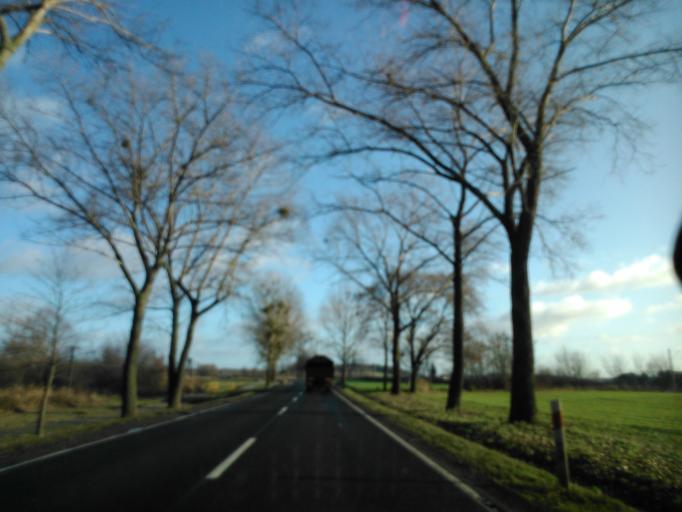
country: PL
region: Kujawsko-Pomorskie
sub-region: Powiat inowroclawski
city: Gniewkowo
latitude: 52.9026
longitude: 18.4532
